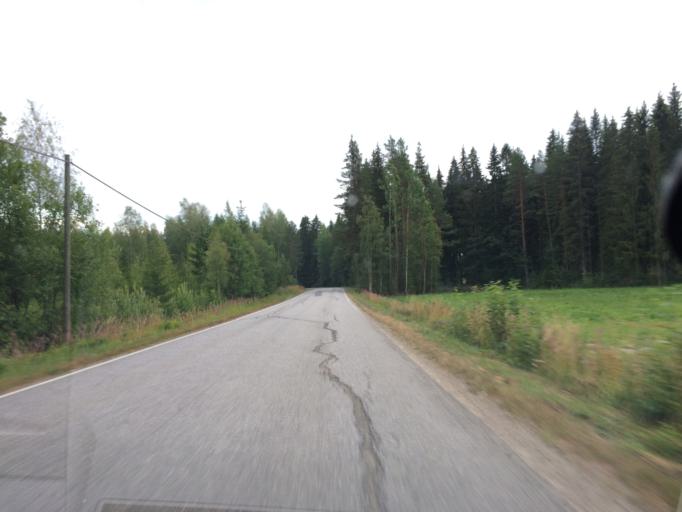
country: FI
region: Haeme
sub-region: Haemeenlinna
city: Tuulos
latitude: 61.1923
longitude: 24.7503
